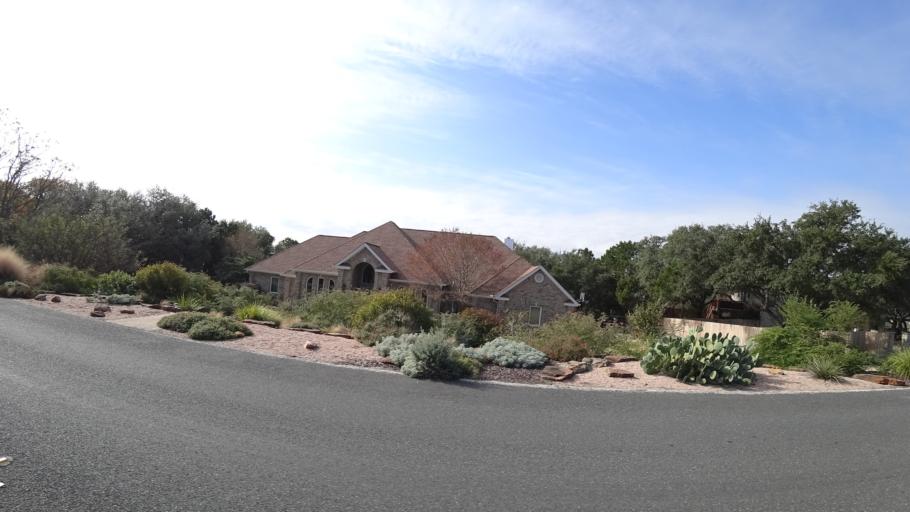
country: US
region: Texas
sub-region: Williamson County
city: Jollyville
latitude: 30.3763
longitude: -97.8191
